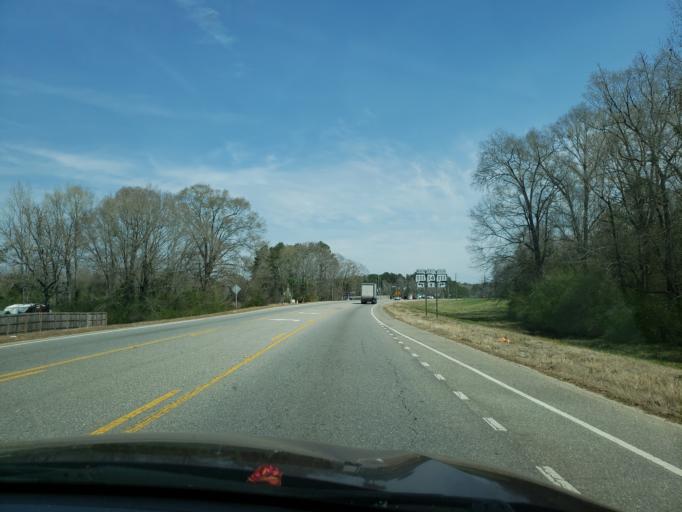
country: US
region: Alabama
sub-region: Elmore County
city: Wetumpka
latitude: 32.5524
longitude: -86.2185
